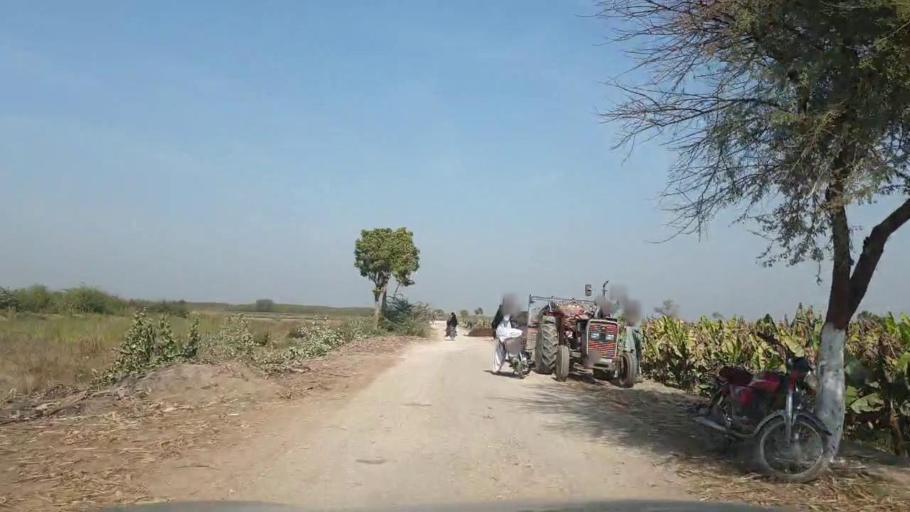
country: PK
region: Sindh
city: Tando Adam
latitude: 25.6298
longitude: 68.7383
